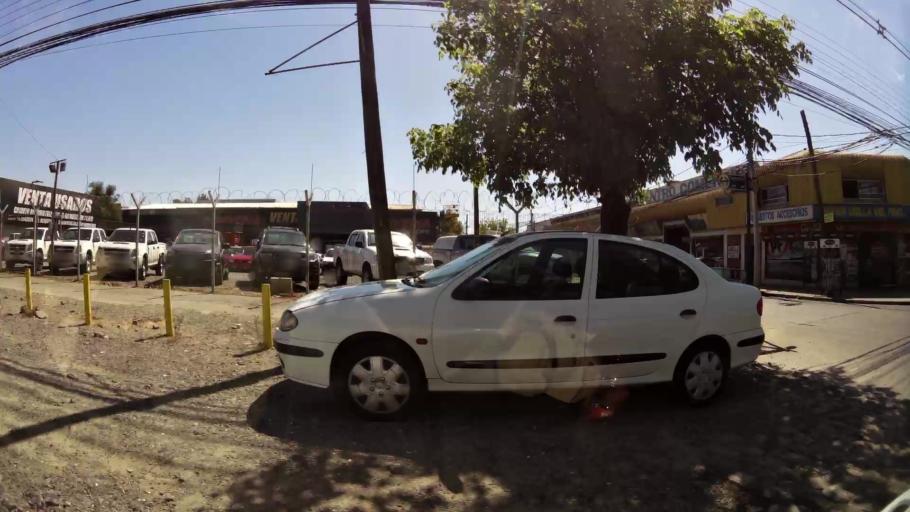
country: CL
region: Maule
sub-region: Provincia de Talca
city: Talca
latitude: -35.4307
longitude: -71.6506
